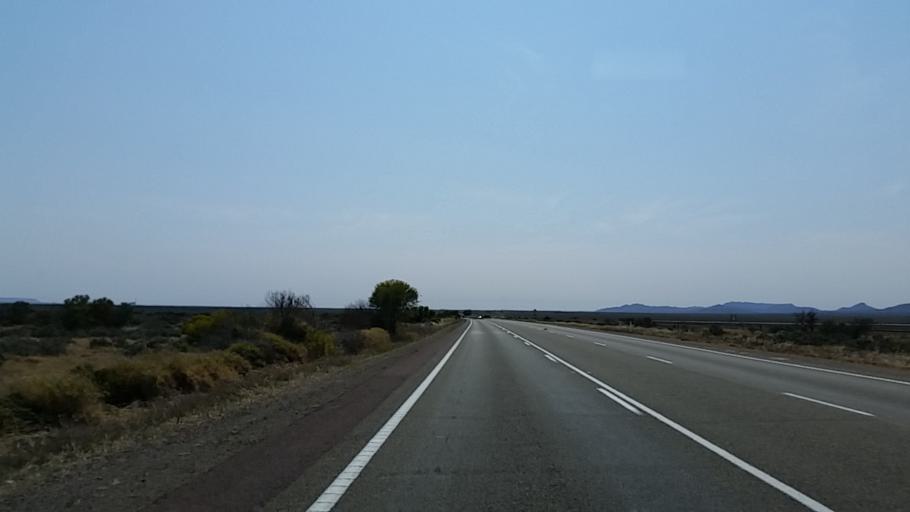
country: AU
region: South Australia
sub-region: Port Augusta
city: Port Augusta
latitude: -32.6831
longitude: 137.9384
